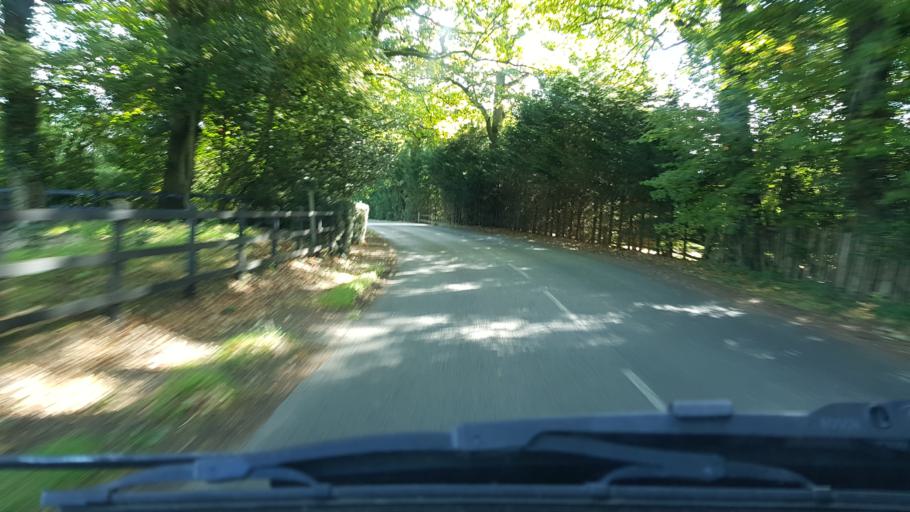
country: GB
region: England
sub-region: West Sussex
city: Rudgwick
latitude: 51.0640
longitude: -0.5339
